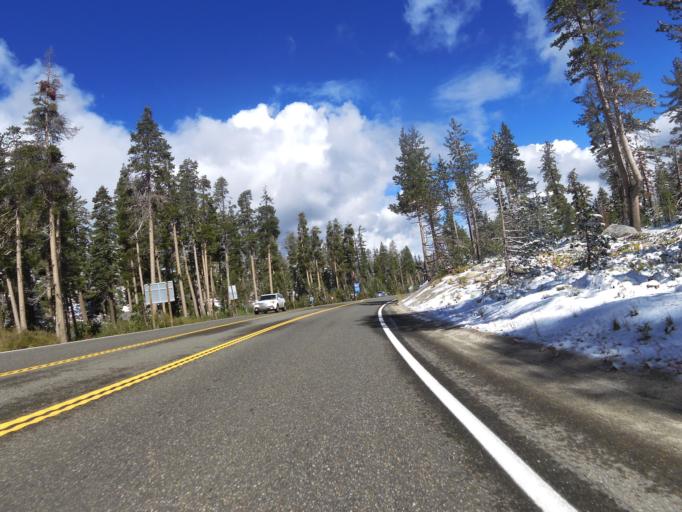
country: US
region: California
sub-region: El Dorado County
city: South Lake Tahoe
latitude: 38.8139
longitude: -120.0331
